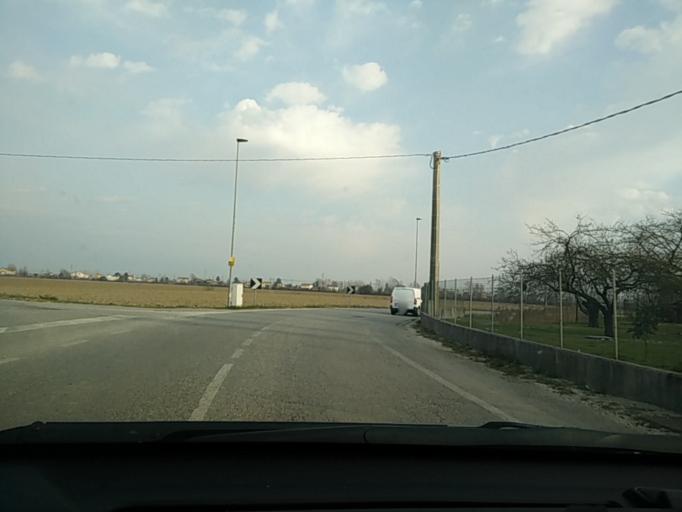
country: IT
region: Veneto
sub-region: Provincia di Venezia
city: Fossalta di Piave
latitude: 45.6281
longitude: 12.5040
